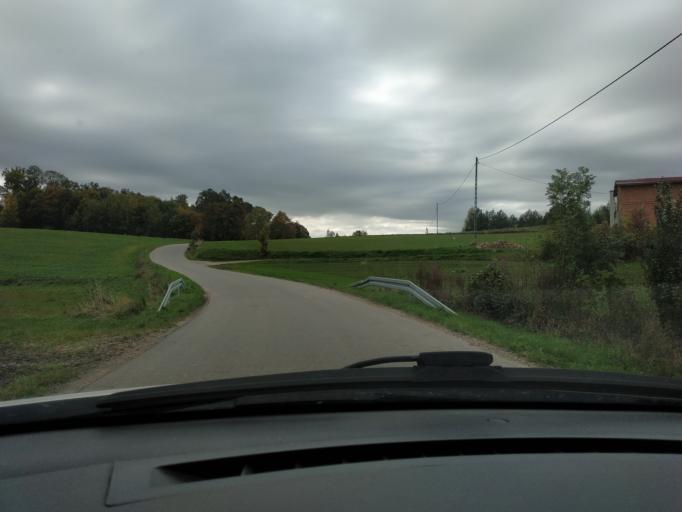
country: PL
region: Warmian-Masurian Voivodeship
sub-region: Powiat nowomiejski
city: Biskupiec
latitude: 53.4563
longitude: 19.3155
